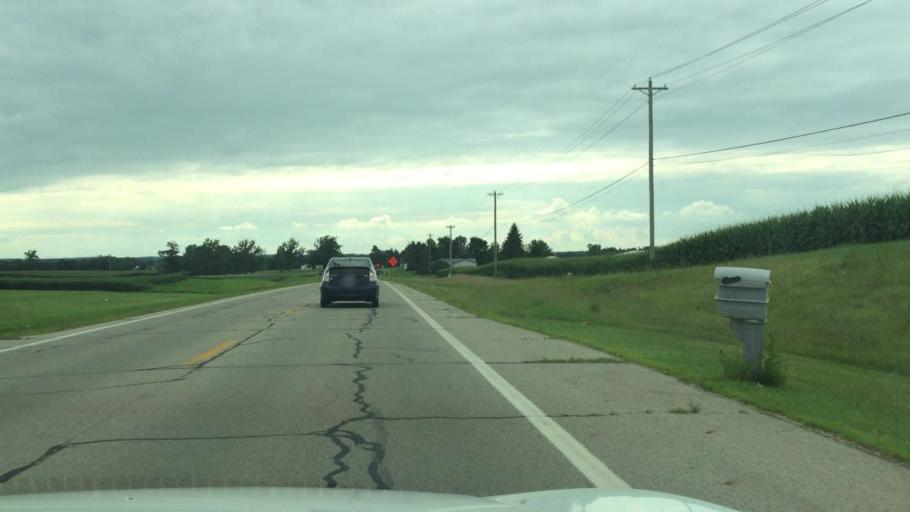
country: US
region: Ohio
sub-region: Champaign County
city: Mechanicsburg
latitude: 40.0785
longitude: -83.6189
